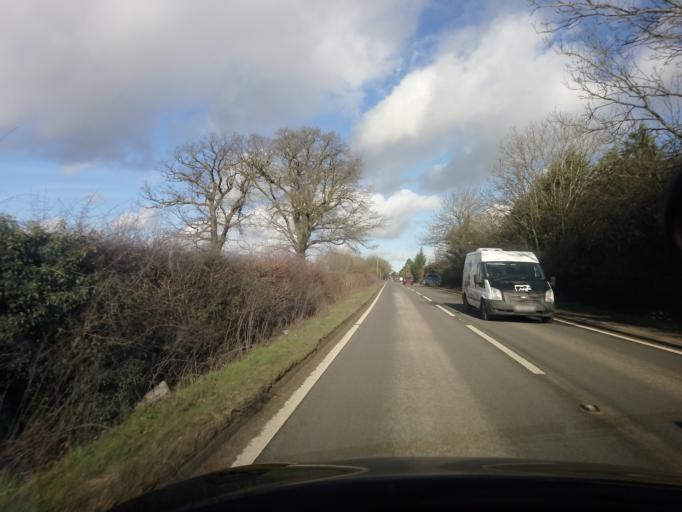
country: GB
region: England
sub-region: Shropshire
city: Astley
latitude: 52.7536
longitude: -2.7166
